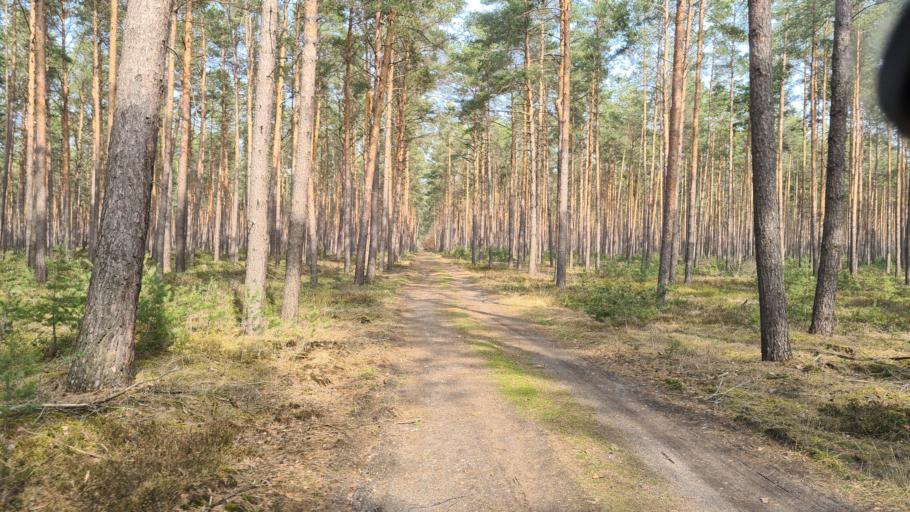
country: DE
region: Brandenburg
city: Trobitz
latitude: 51.6490
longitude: 13.4570
